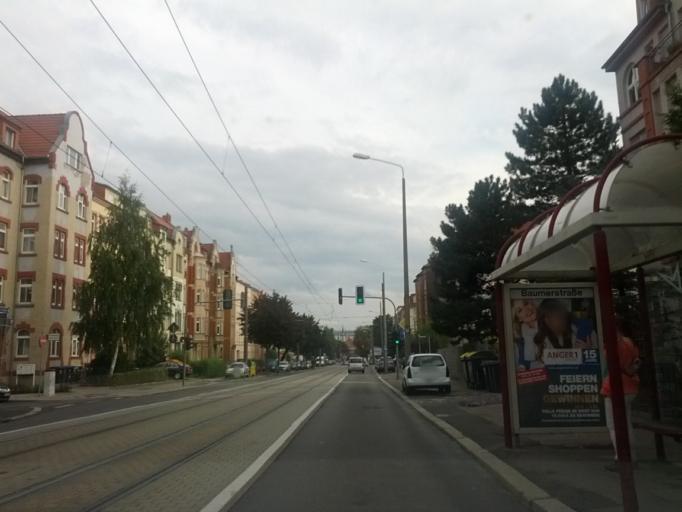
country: DE
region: Thuringia
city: Erfurt
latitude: 50.9865
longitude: 11.0164
